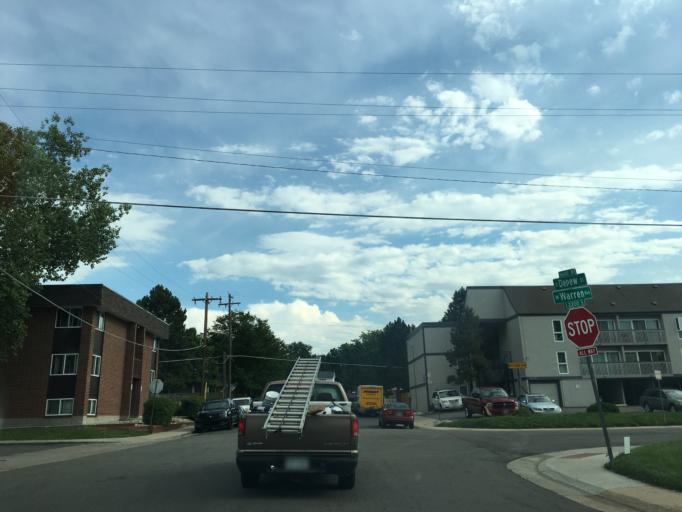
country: US
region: Colorado
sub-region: Jefferson County
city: Lakewood
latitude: 39.6757
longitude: -105.0573
